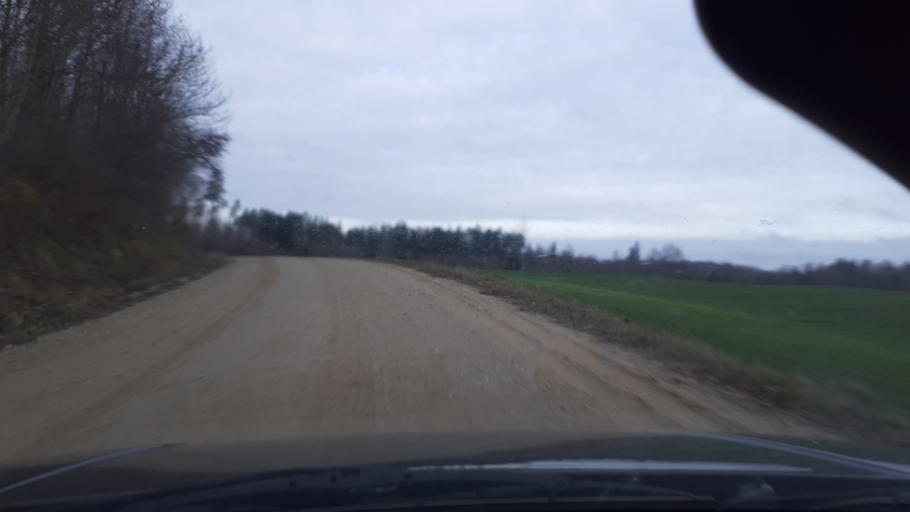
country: LV
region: Alsunga
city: Alsunga
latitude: 56.9598
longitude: 21.6523
